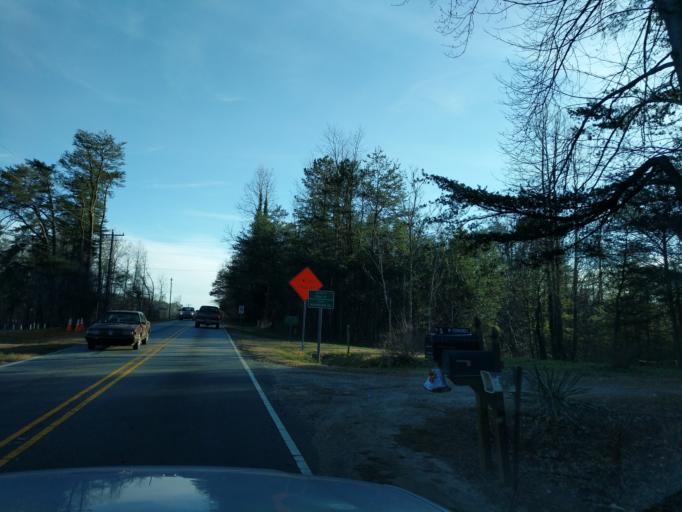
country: US
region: North Carolina
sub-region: Rutherford County
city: Lake Lure
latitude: 35.4023
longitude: -82.1966
